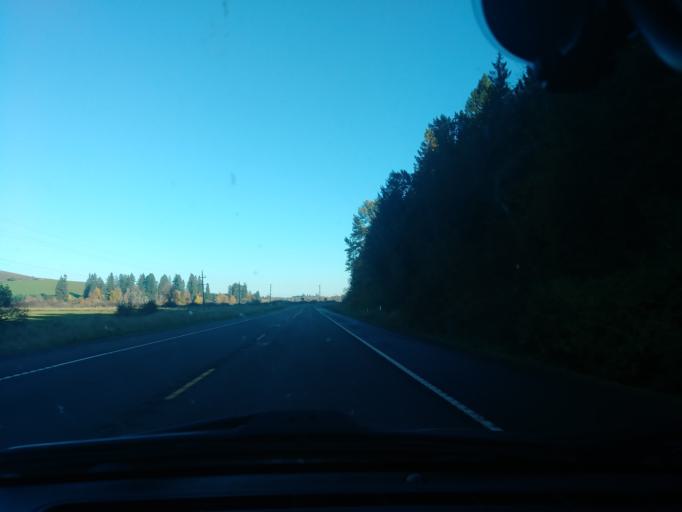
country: US
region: Oregon
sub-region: Washington County
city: Banks
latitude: 45.6143
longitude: -123.1710
